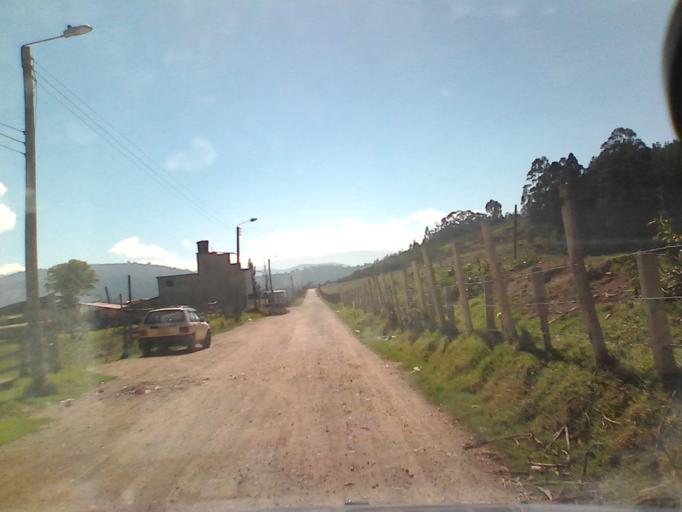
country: CO
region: Boyaca
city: Duitama
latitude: 5.7950
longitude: -73.0406
